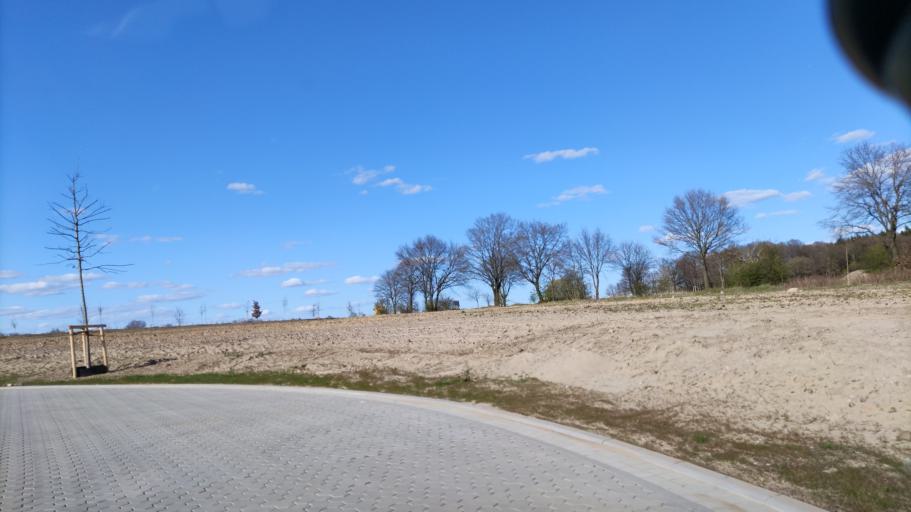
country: DE
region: Lower Saxony
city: Buchholz in der Nordheide
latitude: 53.3597
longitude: 9.8713
